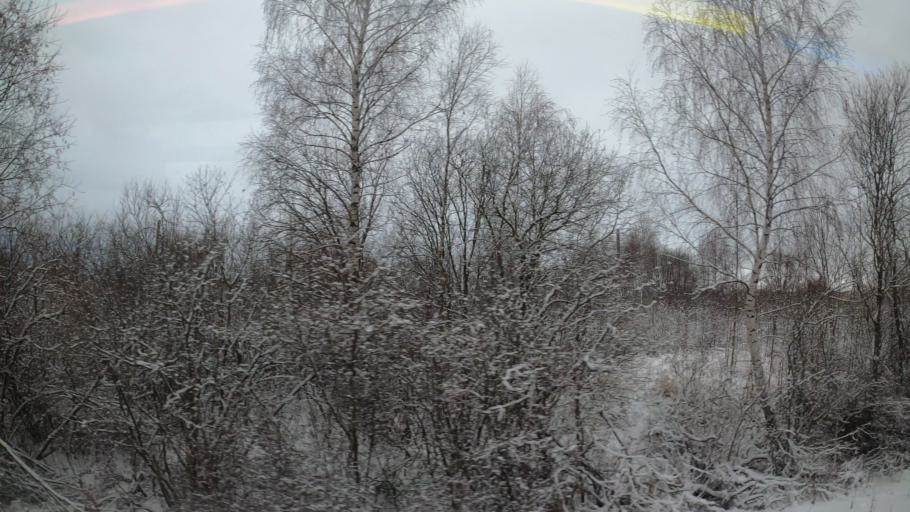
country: RU
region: Jaroslavl
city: Pereslavl'-Zalesskiy
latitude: 56.7294
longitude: 38.9020
